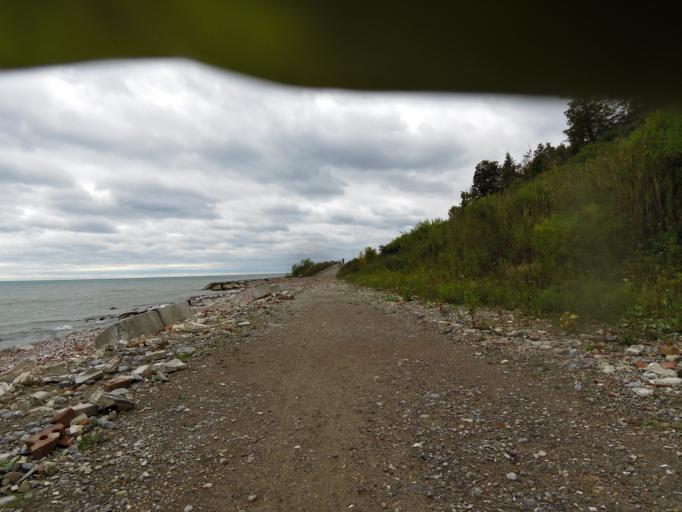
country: CA
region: Ontario
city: Scarborough
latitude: 43.7281
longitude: -79.2130
